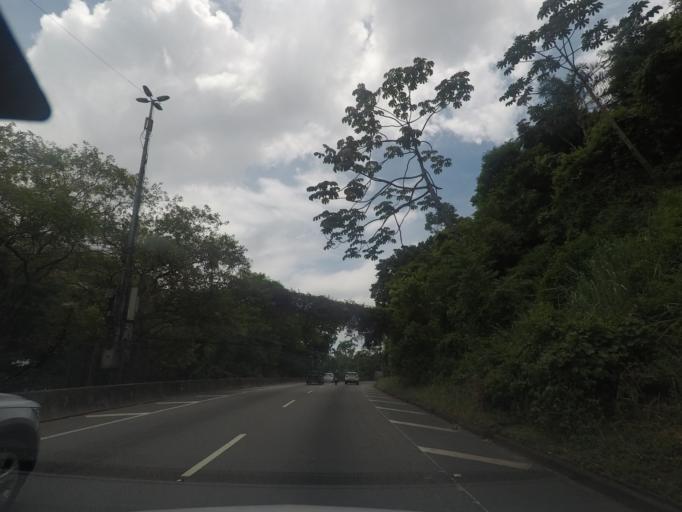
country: BR
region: Rio de Janeiro
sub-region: Rio De Janeiro
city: Rio de Janeiro
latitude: -22.9834
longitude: -43.2379
